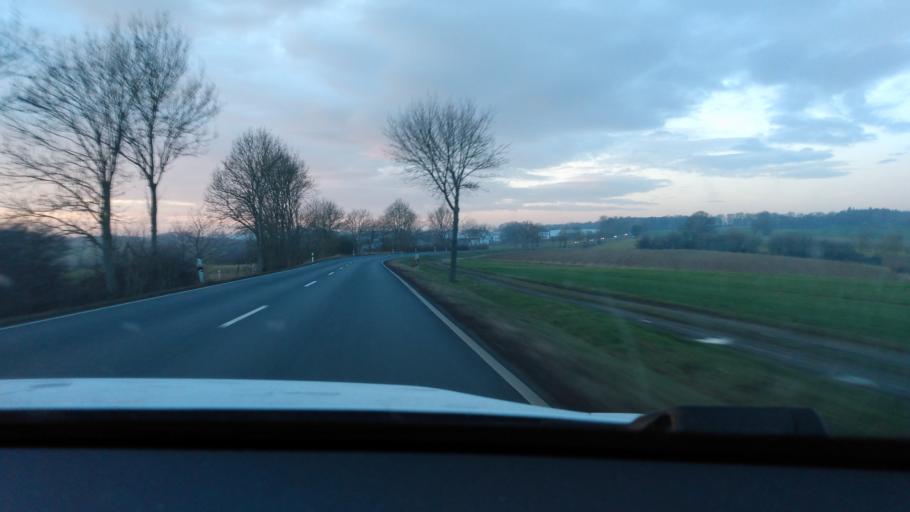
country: DE
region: Rheinland-Pfalz
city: Kircheib
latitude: 50.7092
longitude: 7.4210
